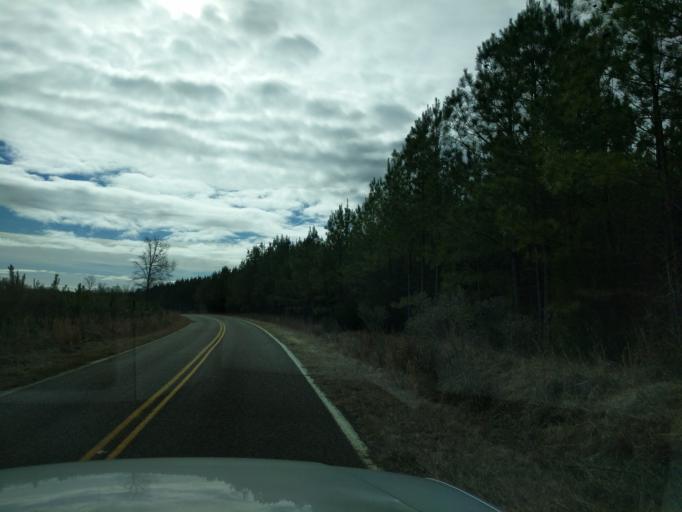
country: US
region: South Carolina
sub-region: Edgefield County
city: Edgefield
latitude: 33.9197
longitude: -82.0070
